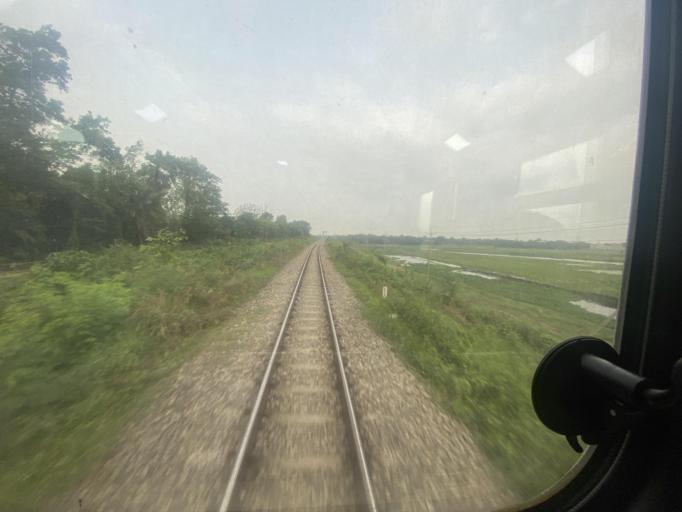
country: BD
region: Dhaka
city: Tungi
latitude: 23.9341
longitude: 90.4936
